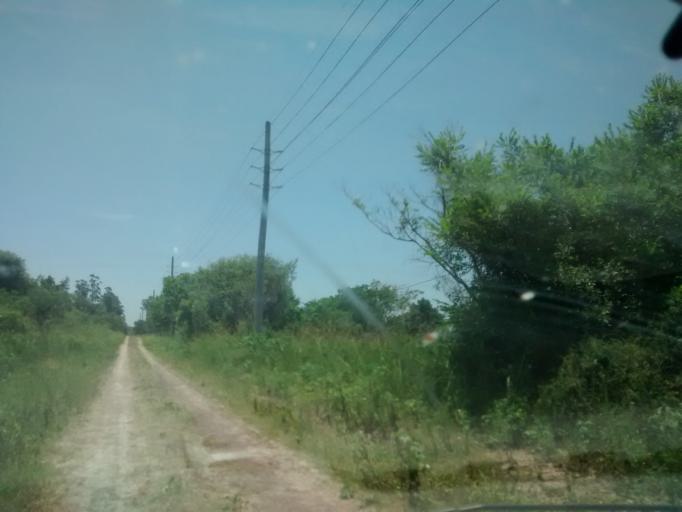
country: AR
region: Chaco
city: Fontana
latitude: -27.4219
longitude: -58.9880
